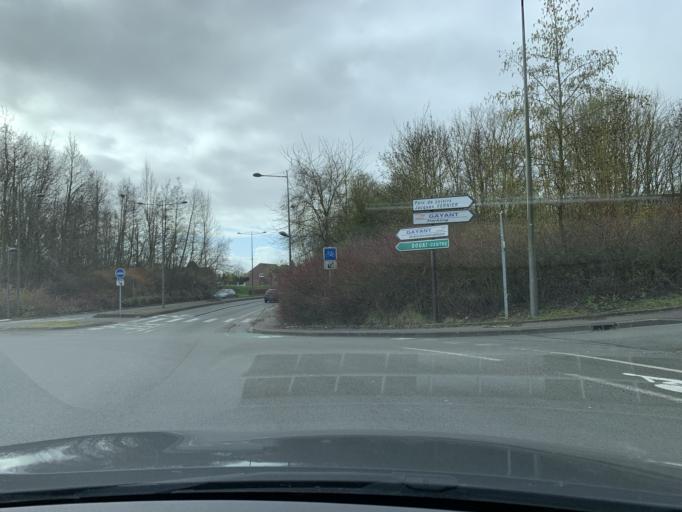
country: FR
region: Nord-Pas-de-Calais
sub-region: Departement du Nord
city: Waziers
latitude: 50.3840
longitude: 3.0970
